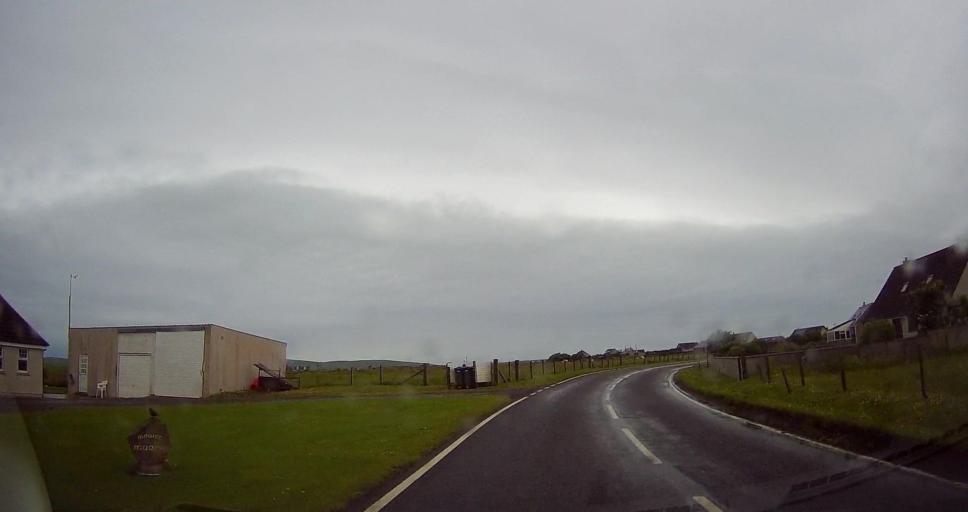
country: GB
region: Scotland
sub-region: Orkney Islands
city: Stromness
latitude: 59.0706
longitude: -3.2352
